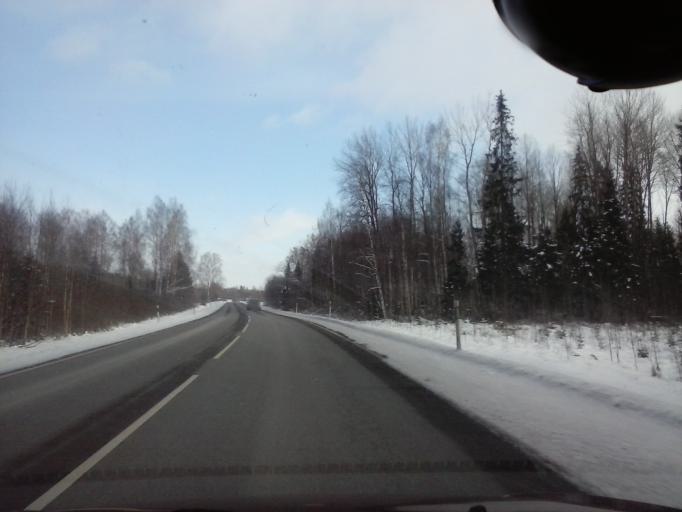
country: EE
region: Jogevamaa
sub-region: Poltsamaa linn
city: Poltsamaa
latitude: 58.3894
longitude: 25.9255
